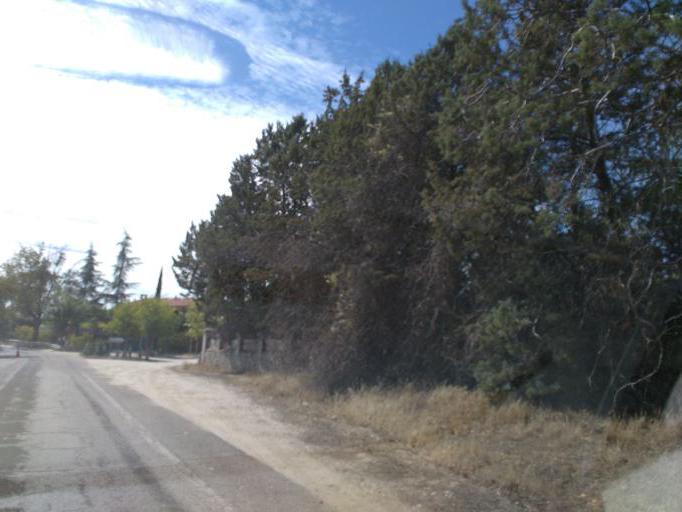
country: ES
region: Madrid
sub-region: Provincia de Madrid
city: Villanueva del Pardillo
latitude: 40.5206
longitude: -3.9414
